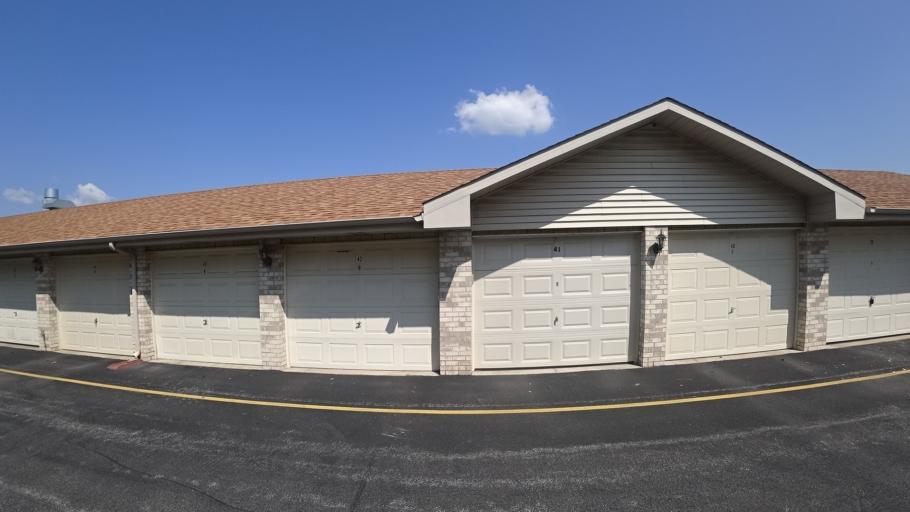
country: US
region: Illinois
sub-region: Cook County
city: Tinley Park
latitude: 41.6137
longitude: -87.7882
